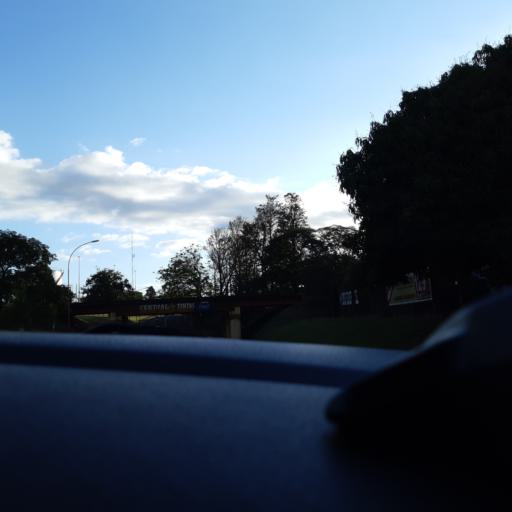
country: BR
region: Sao Paulo
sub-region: Ourinhos
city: Ourinhos
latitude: -22.9848
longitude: -49.8582
